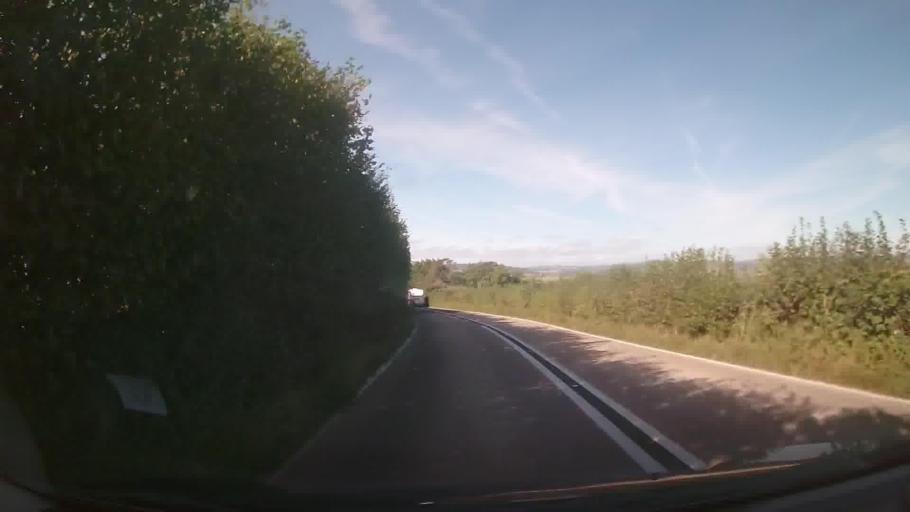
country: GB
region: Wales
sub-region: Sir Powys
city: Hay
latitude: 51.9814
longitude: -3.2234
